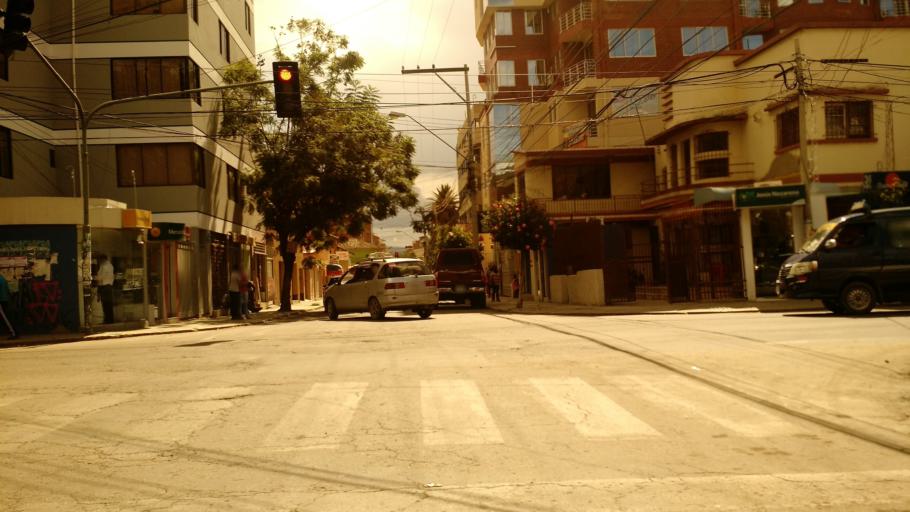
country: BO
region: Cochabamba
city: Cochabamba
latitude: -17.3918
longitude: -66.1485
